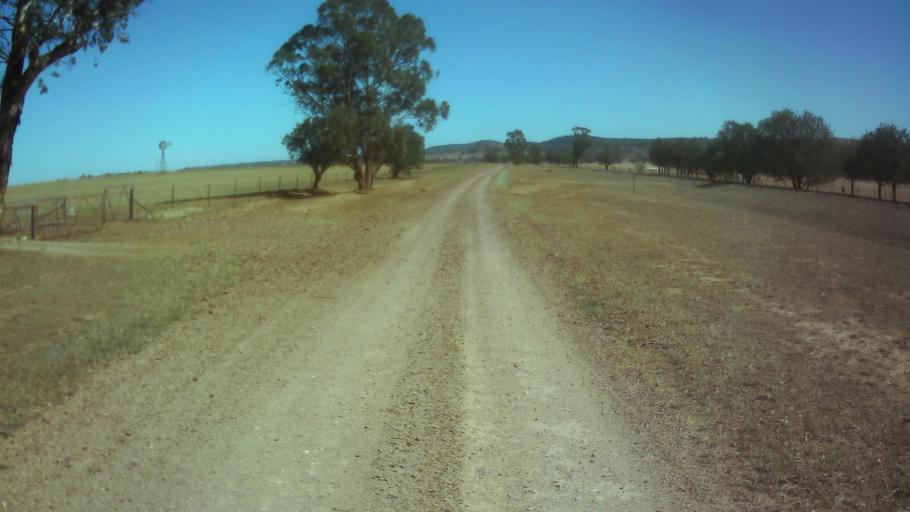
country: AU
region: New South Wales
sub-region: Weddin
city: Grenfell
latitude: -33.9599
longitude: 148.3038
